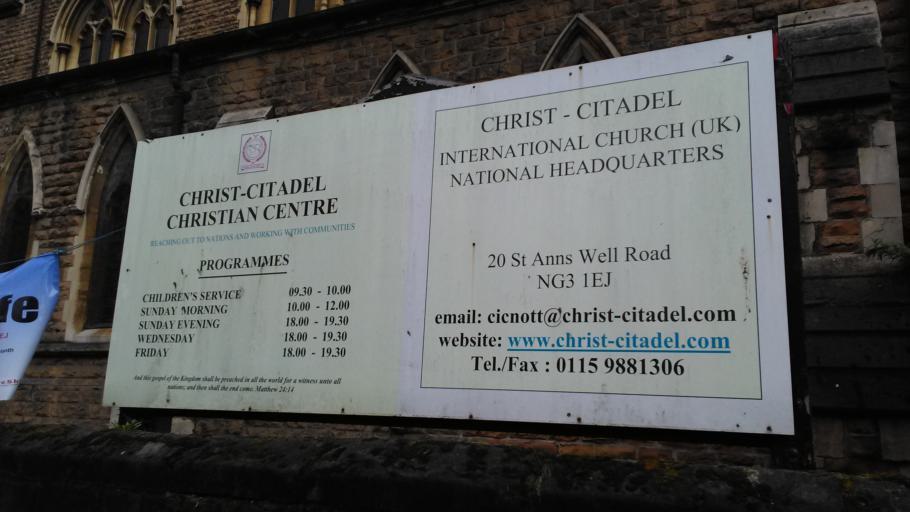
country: GB
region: England
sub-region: Nottingham
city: Nottingham
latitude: 52.9576
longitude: -1.1421
